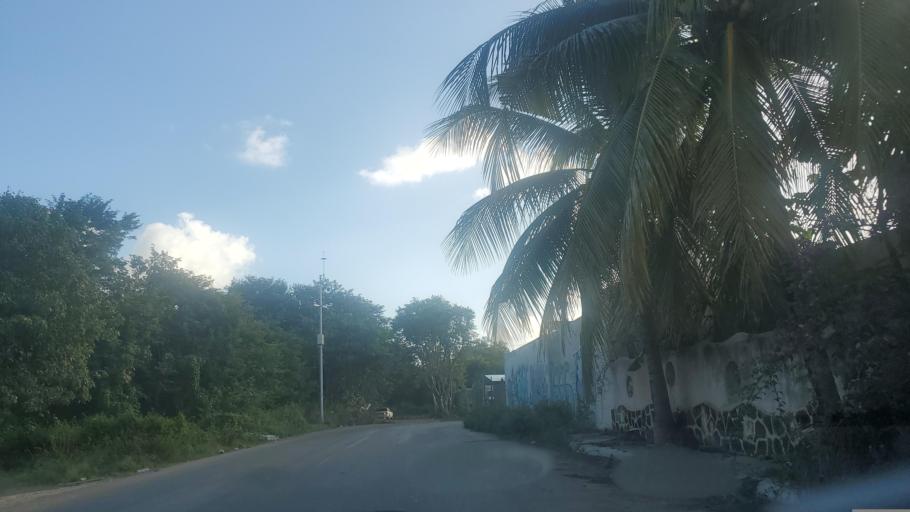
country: MX
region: Quintana Roo
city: Tulum
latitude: 20.2181
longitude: -87.4522
